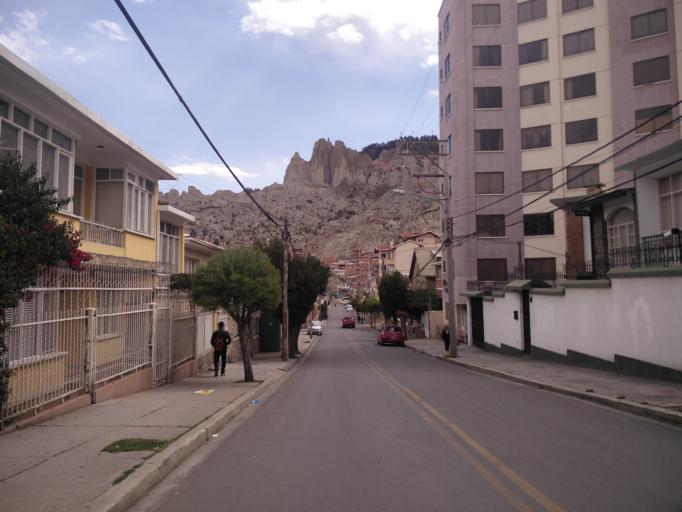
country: BO
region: La Paz
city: La Paz
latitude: -16.5186
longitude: -68.1300
